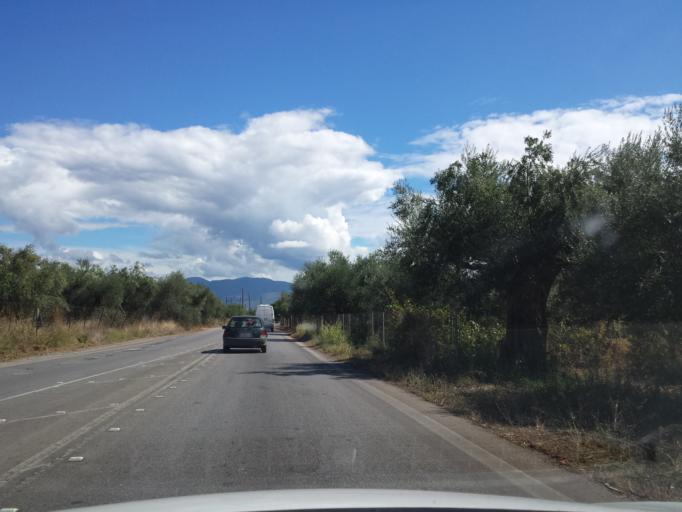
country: GR
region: Peloponnese
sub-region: Nomos Messinias
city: Messini
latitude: 37.0241
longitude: 21.9715
